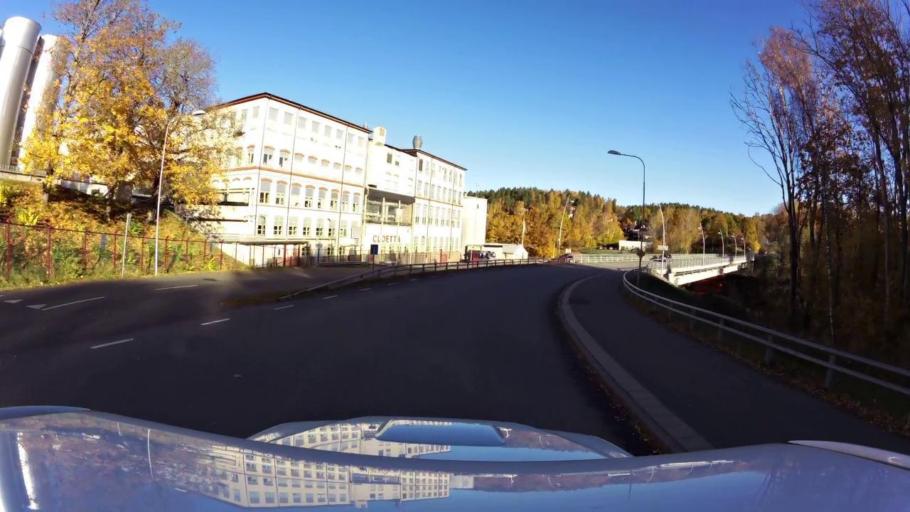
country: SE
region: OEstergoetland
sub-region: Linkopings Kommun
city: Ljungsbro
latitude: 58.5132
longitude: 15.5022
